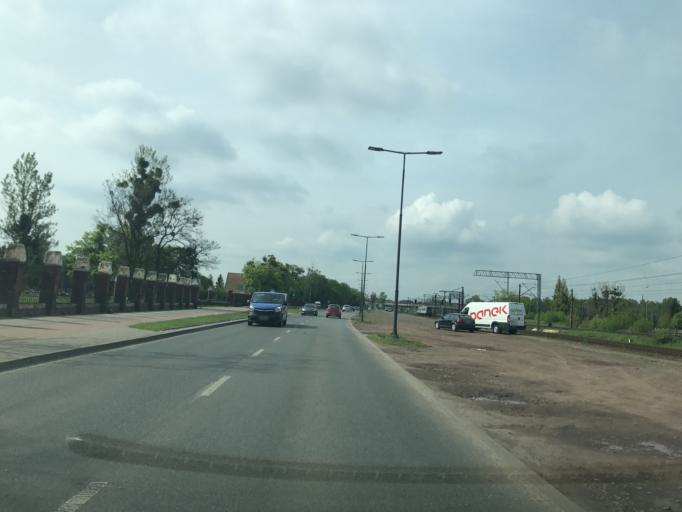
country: PL
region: Kujawsko-Pomorskie
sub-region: Bydgoszcz
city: Bydgoszcz
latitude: 53.1436
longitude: 18.0052
